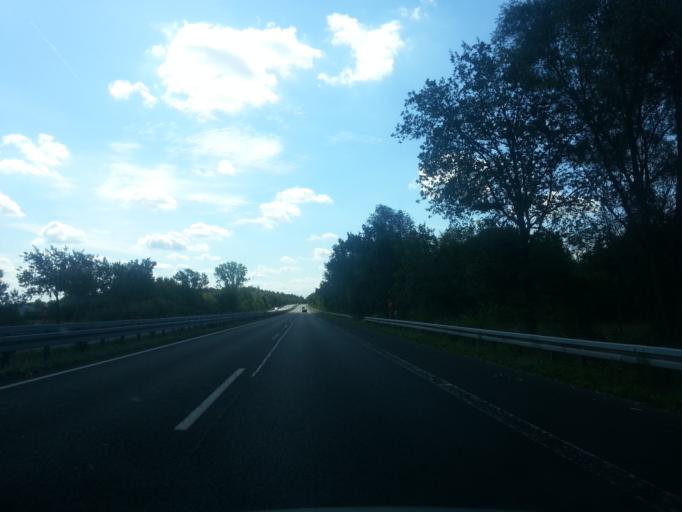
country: DE
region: Hesse
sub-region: Regierungsbezirk Darmstadt
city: Eppertshausen
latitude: 49.9447
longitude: 8.8348
